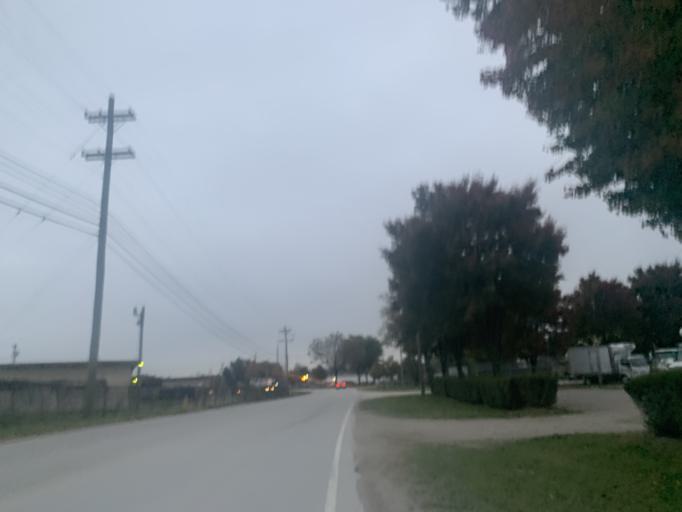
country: US
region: Kentucky
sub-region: Jefferson County
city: Shively
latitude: 38.2161
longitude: -85.8083
